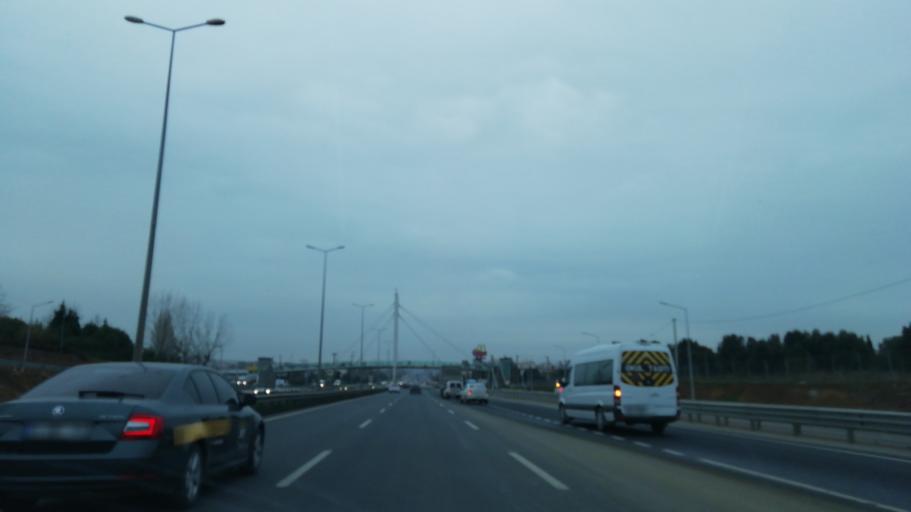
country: TR
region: Kocaeli
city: Darica
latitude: 40.8127
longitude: 29.3668
